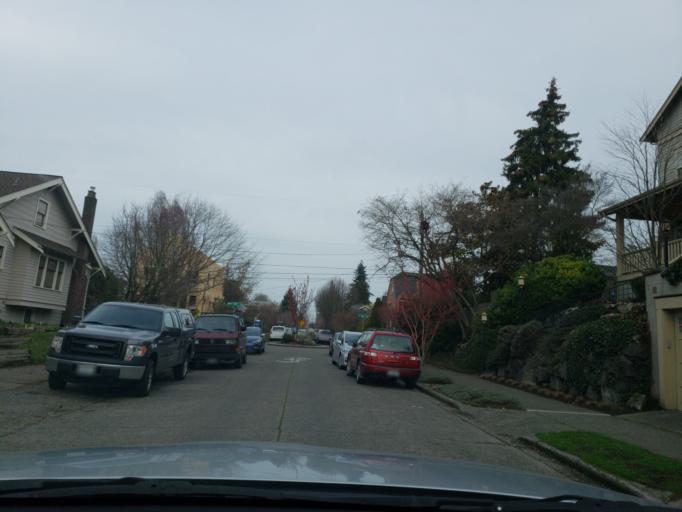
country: US
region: Washington
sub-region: King County
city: Shoreline
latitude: 47.6821
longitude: -122.3580
